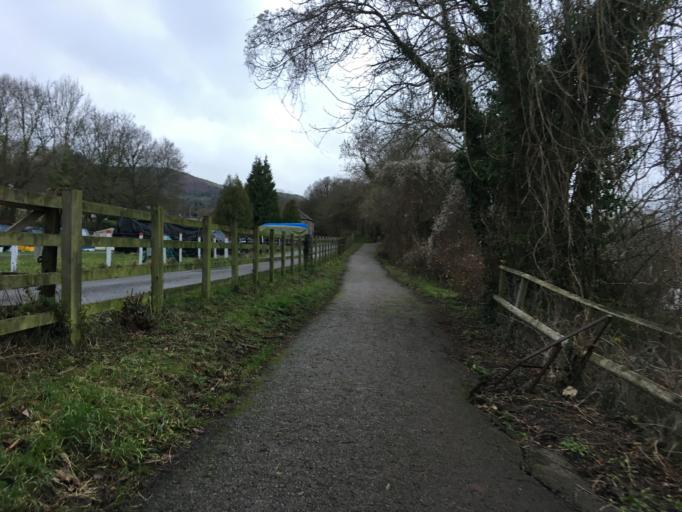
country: GB
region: Wales
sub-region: Monmouthshire
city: Gilwern
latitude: 51.8173
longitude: -3.0591
